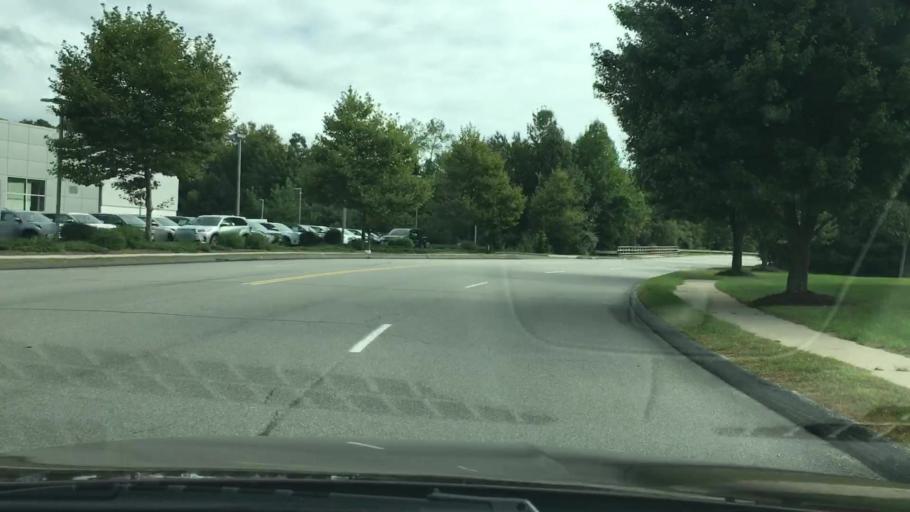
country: US
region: Connecticut
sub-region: Middlesex County
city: Westbrook Center
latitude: 41.2900
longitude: -72.4430
